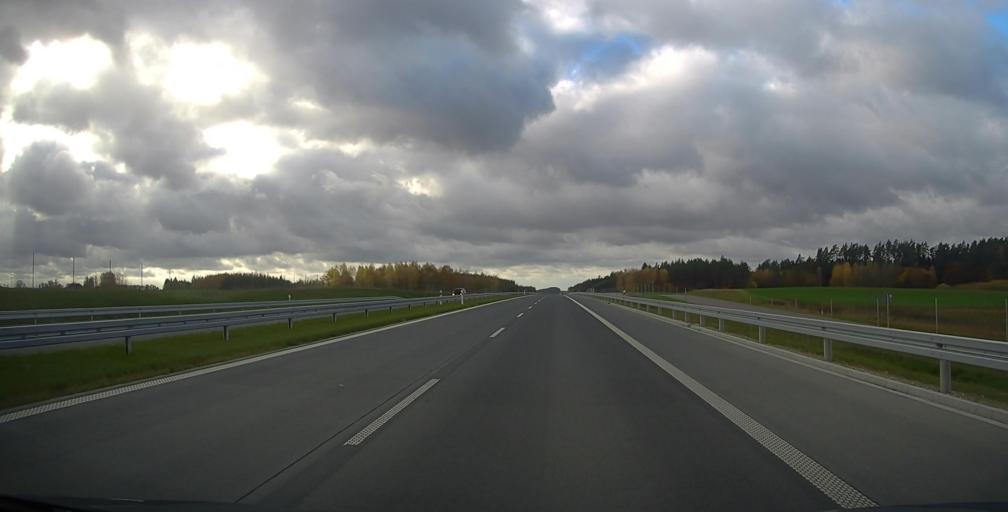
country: PL
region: Podlasie
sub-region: Powiat grajewski
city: Rajgrod
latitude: 53.8739
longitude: 22.6479
